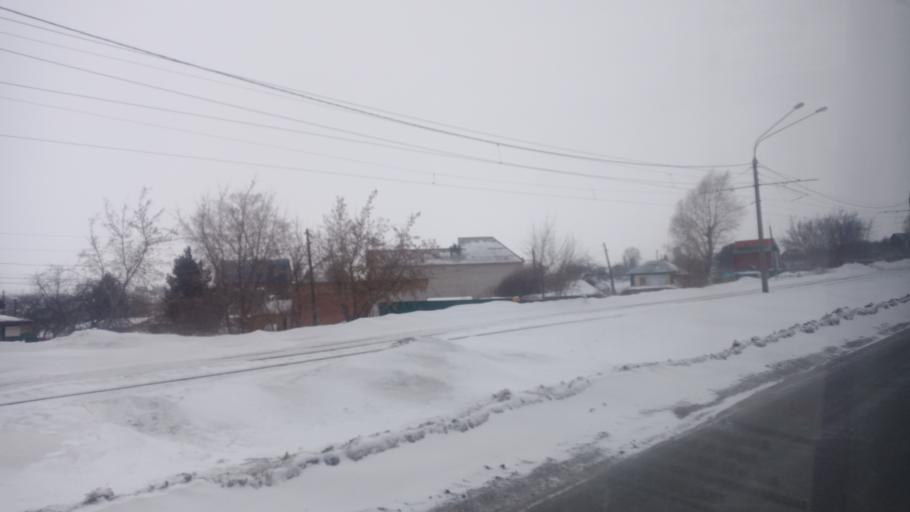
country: RU
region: Altai Krai
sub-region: Gorod Barnaulskiy
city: Barnaul
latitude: 53.3883
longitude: 83.6800
